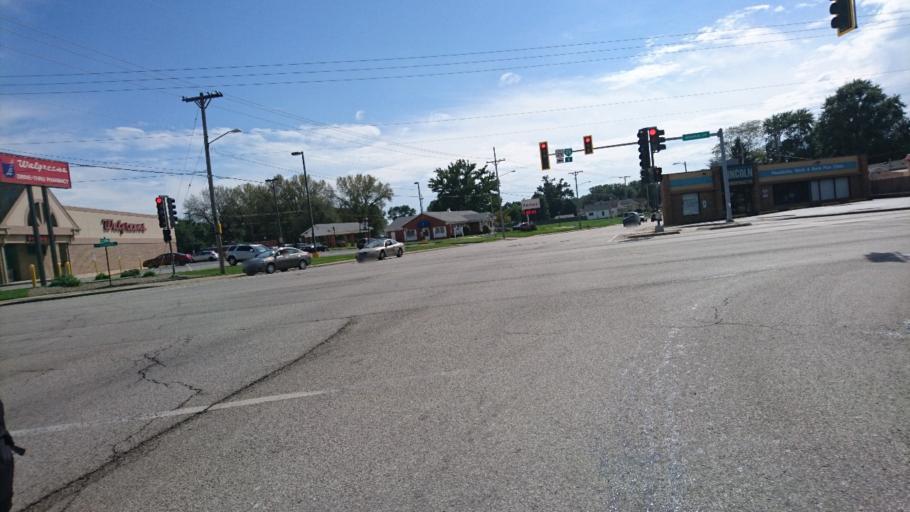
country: US
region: Illinois
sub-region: Sangamon County
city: Grandview
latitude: 39.8313
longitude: -89.6365
